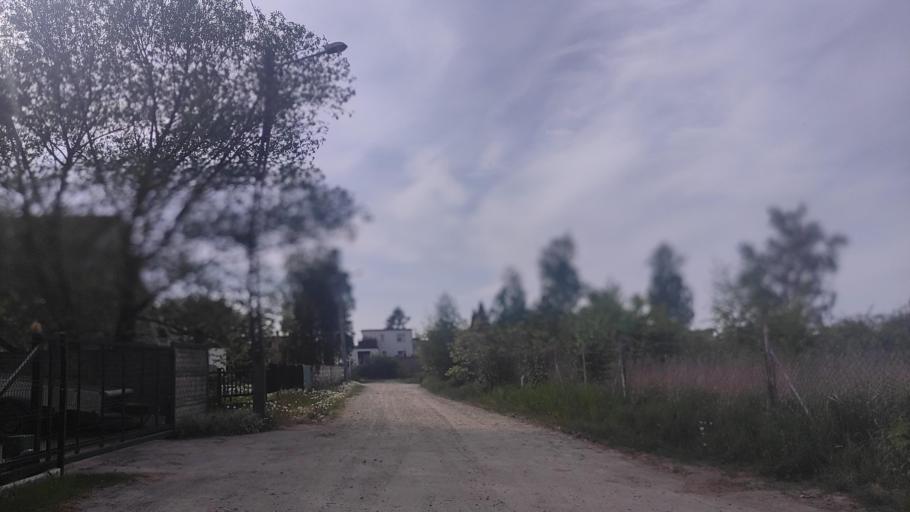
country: PL
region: Greater Poland Voivodeship
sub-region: Powiat poznanski
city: Swarzedz
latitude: 52.4123
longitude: 17.0952
